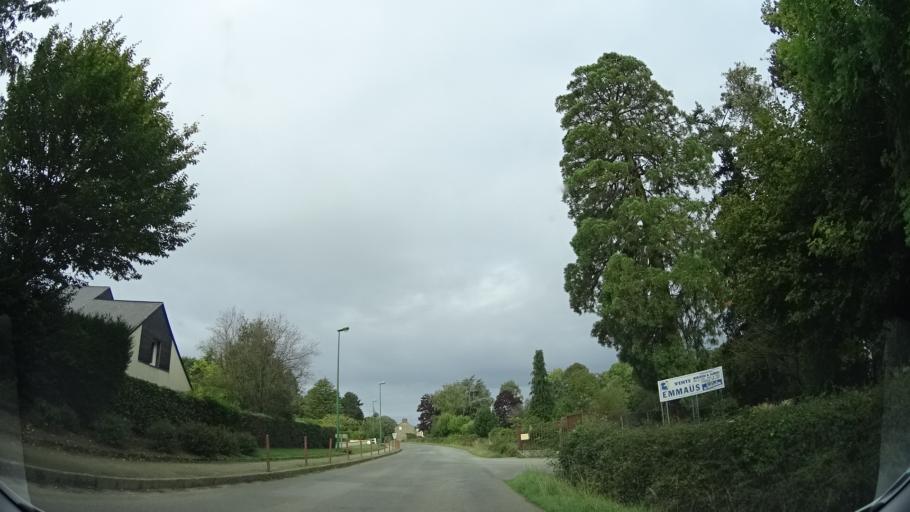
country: FR
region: Brittany
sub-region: Departement d'Ille-et-Vilaine
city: Hede-Bazouges
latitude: 48.2967
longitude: -1.7941
